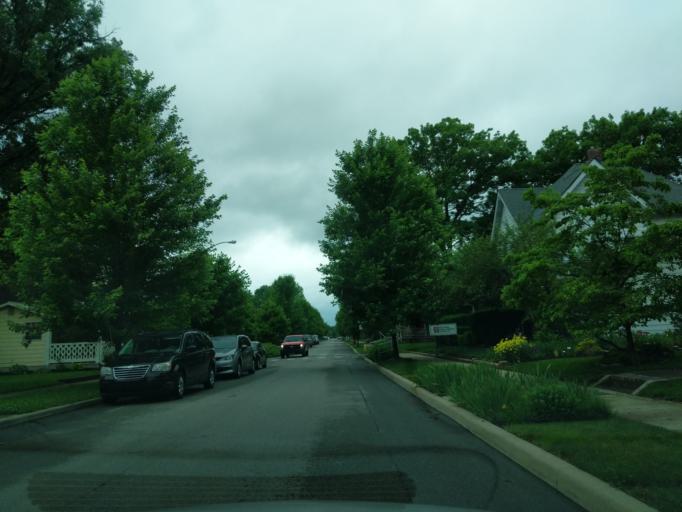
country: US
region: Indiana
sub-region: Hamilton County
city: Noblesville
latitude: 40.0447
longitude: -86.0082
